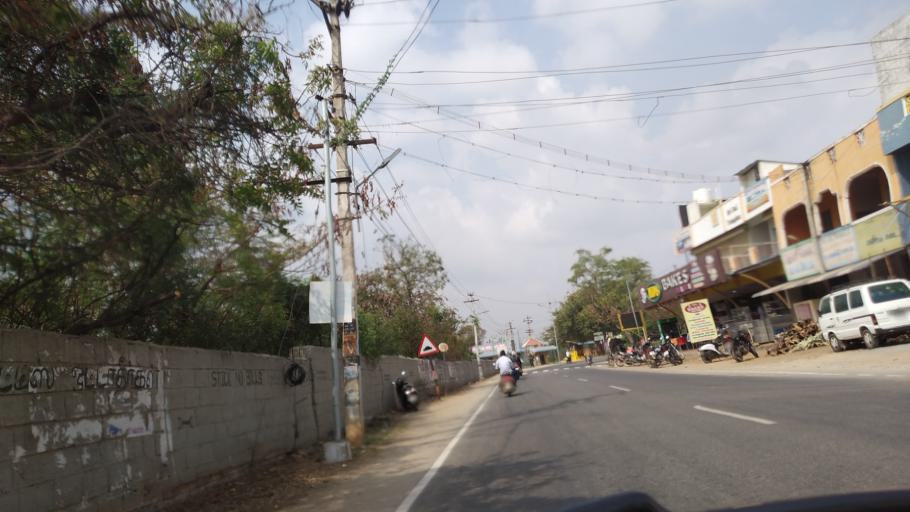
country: IN
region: Tamil Nadu
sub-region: Coimbatore
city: Madukkarai
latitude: 10.9398
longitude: 76.9443
